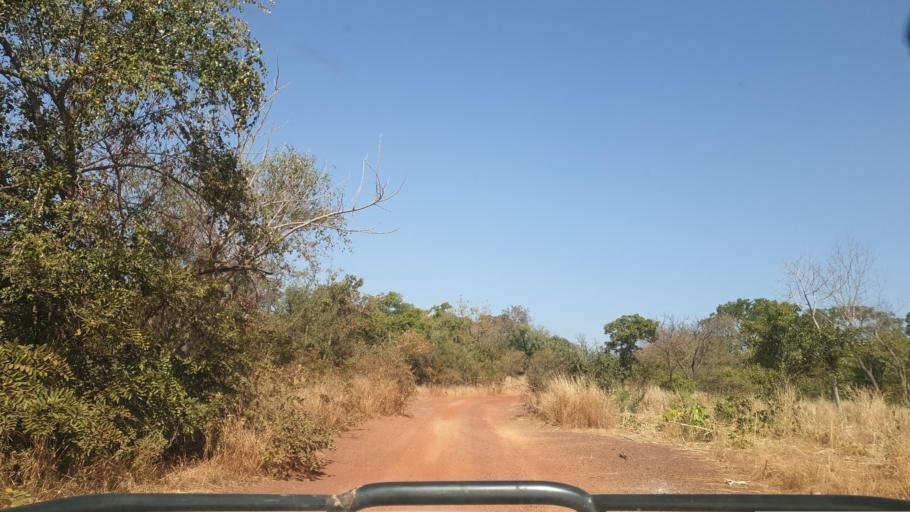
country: ML
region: Koulikoro
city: Dioila
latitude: 11.9112
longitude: -6.9846
